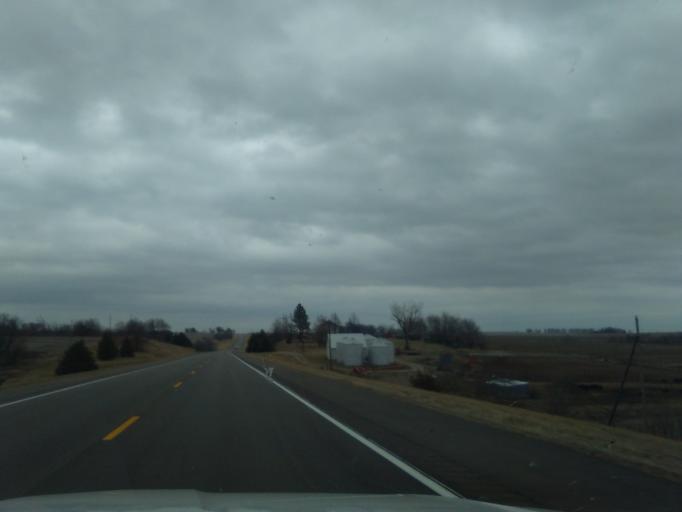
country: US
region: Nebraska
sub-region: Nemaha County
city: Auburn
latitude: 40.3928
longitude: -95.7743
